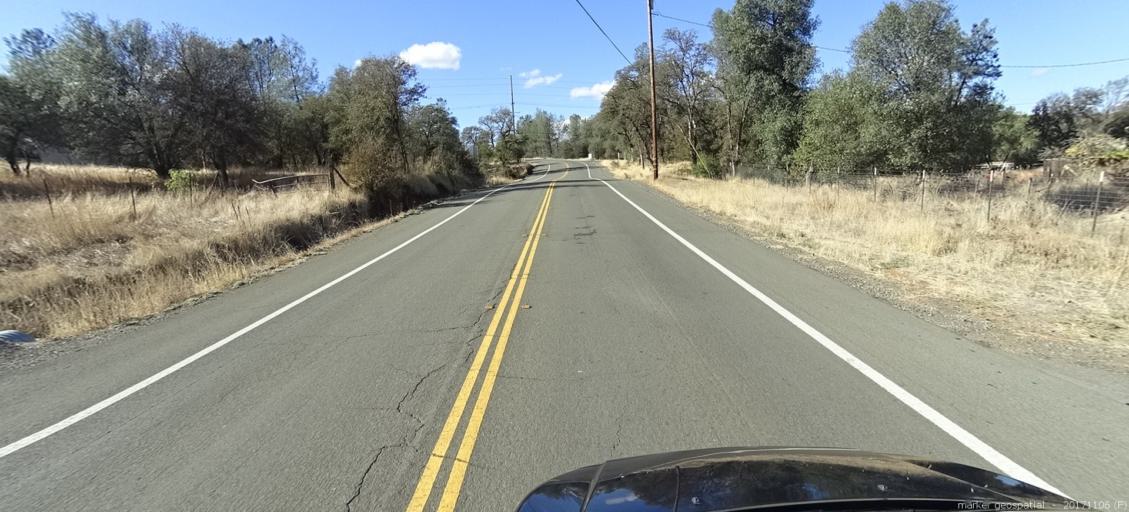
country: US
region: California
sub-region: Shasta County
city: Redding
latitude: 40.5884
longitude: -122.3136
